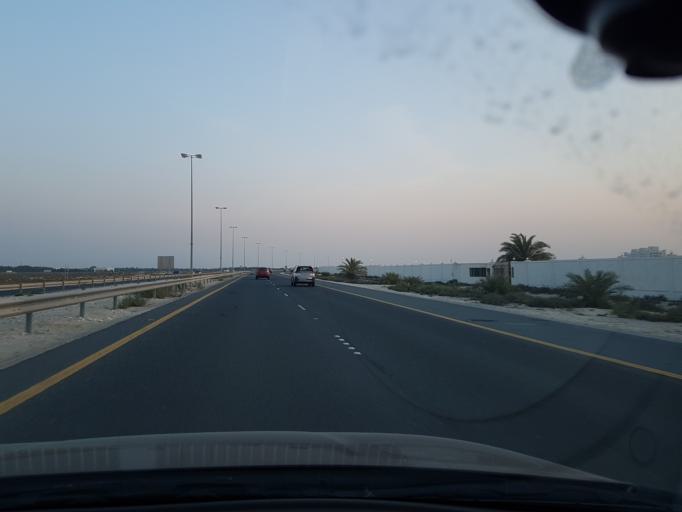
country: BH
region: Central Governorate
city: Dar Kulayb
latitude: 26.0359
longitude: 50.4998
